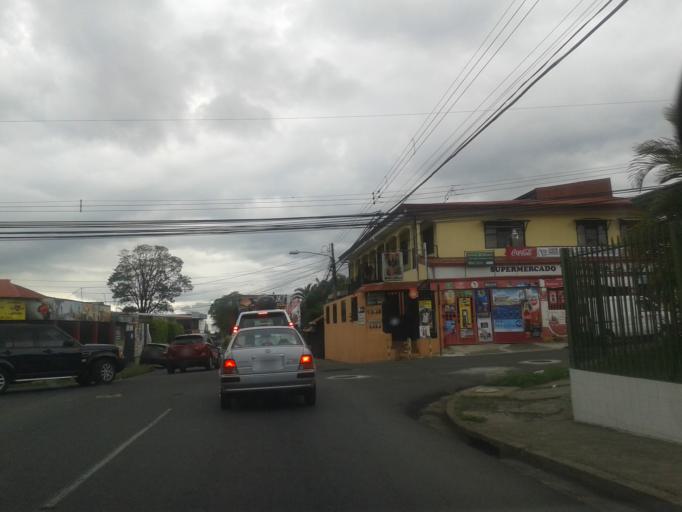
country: CR
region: San Jose
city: San Juan
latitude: 9.9634
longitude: -84.0852
